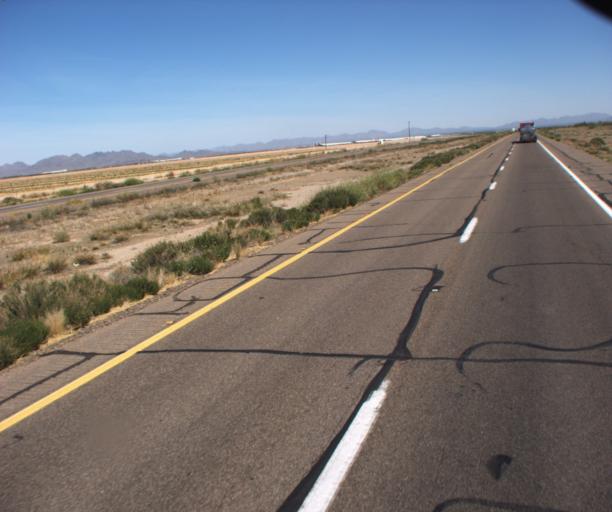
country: US
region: Arizona
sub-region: Maricopa County
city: Gila Bend
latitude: 32.9271
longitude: -112.8472
